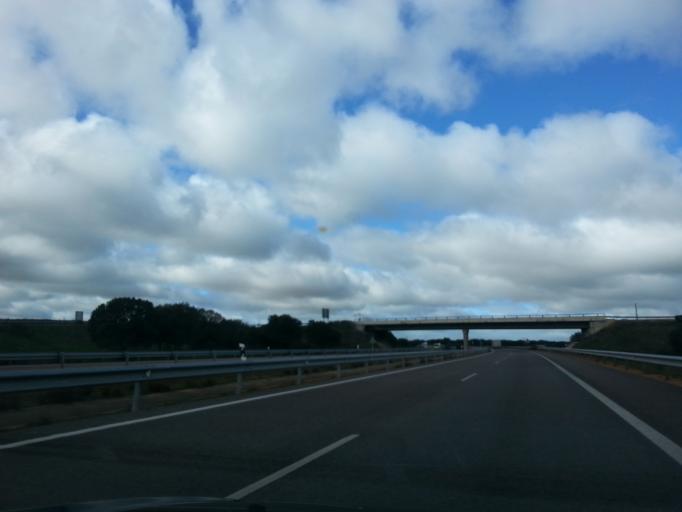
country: ES
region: Castille and Leon
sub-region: Provincia de Salamanca
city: Carrascal de Barregas
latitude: 40.9361
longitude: -5.7873
